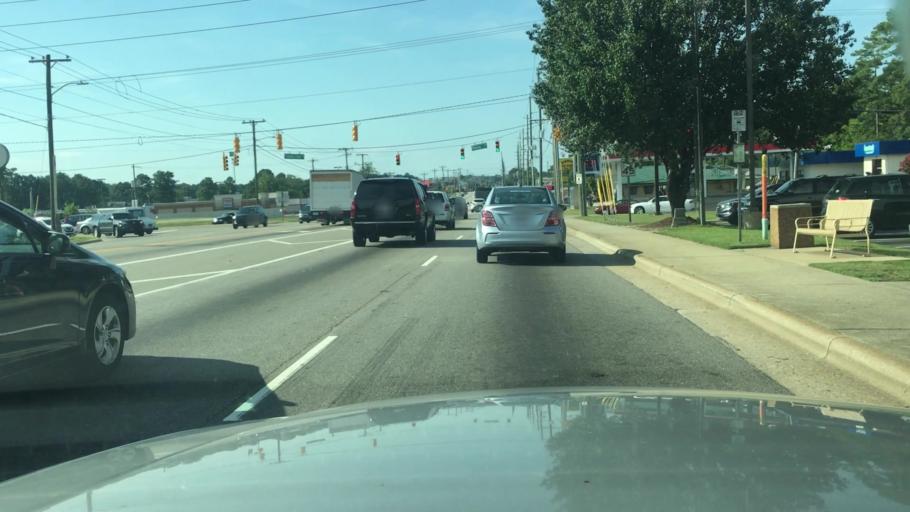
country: US
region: North Carolina
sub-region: Cumberland County
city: Fayetteville
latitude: 35.1045
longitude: -78.8783
